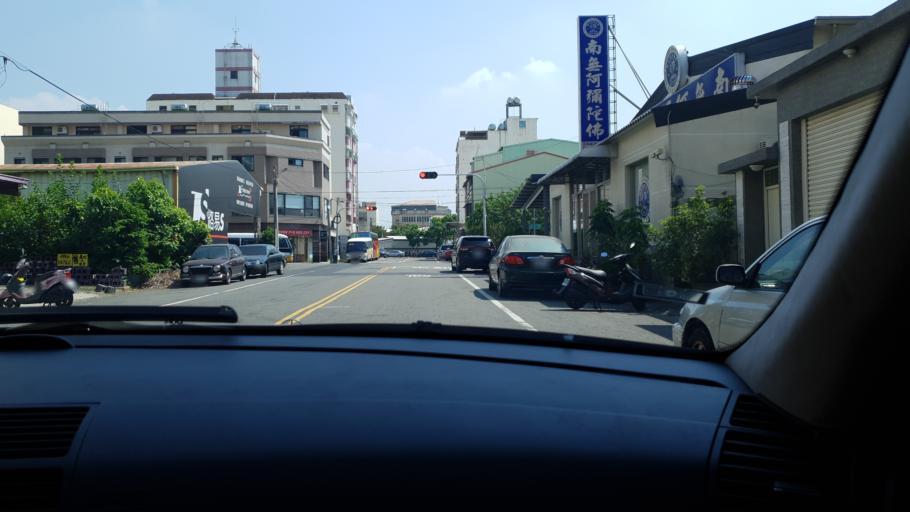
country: TW
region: Taiwan
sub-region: Yunlin
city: Douliu
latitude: 23.7125
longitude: 120.5390
